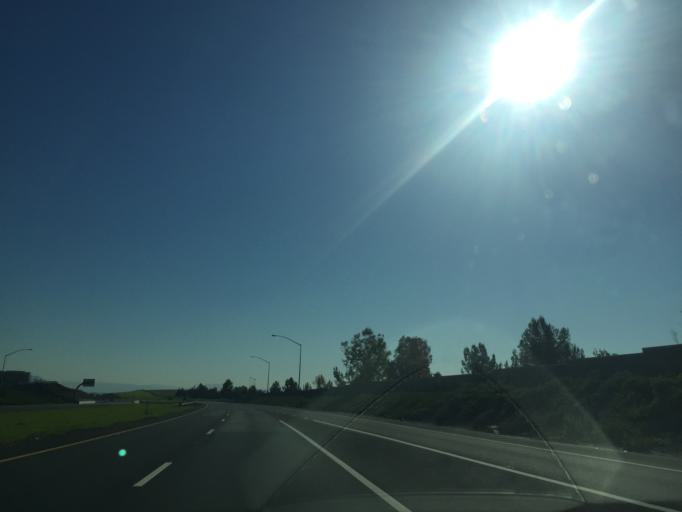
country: US
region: California
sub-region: San Diego County
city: Bonita
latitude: 32.6173
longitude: -116.9715
